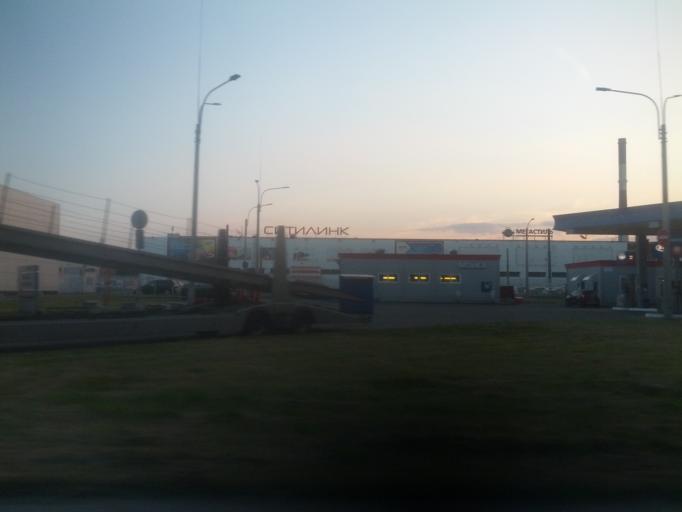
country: RU
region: St.-Petersburg
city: Staraya Derevnya
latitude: 59.9920
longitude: 30.2556
